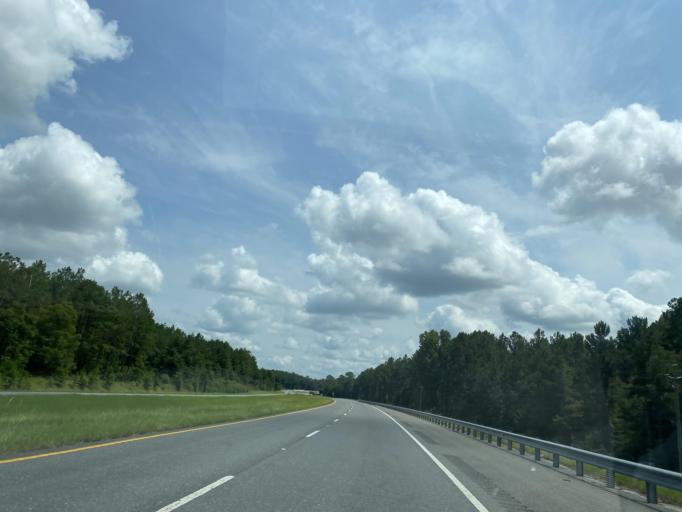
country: US
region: Georgia
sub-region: Ware County
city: Deenwood
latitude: 31.3257
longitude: -82.4622
